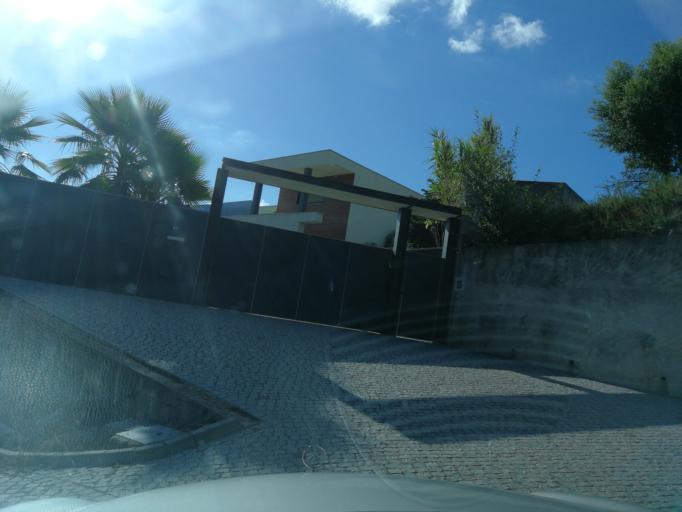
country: PT
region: Braga
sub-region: Braga
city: Adaufe
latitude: 41.5738
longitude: -8.3757
